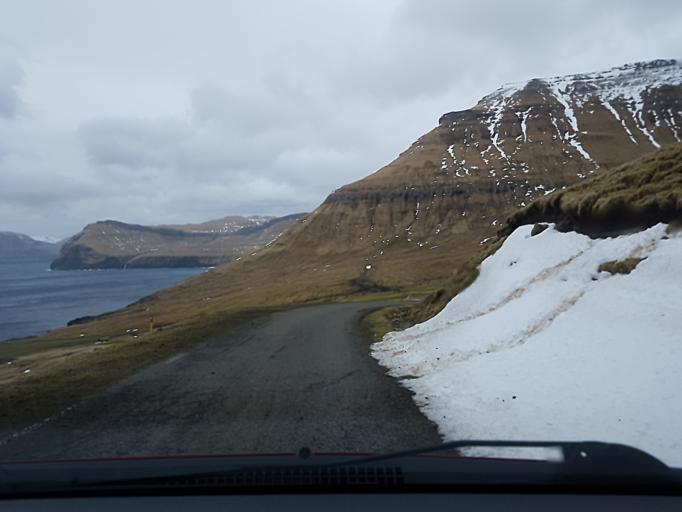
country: FO
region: Streymoy
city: Kollafjordhur
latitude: 62.0205
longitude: -6.9096
